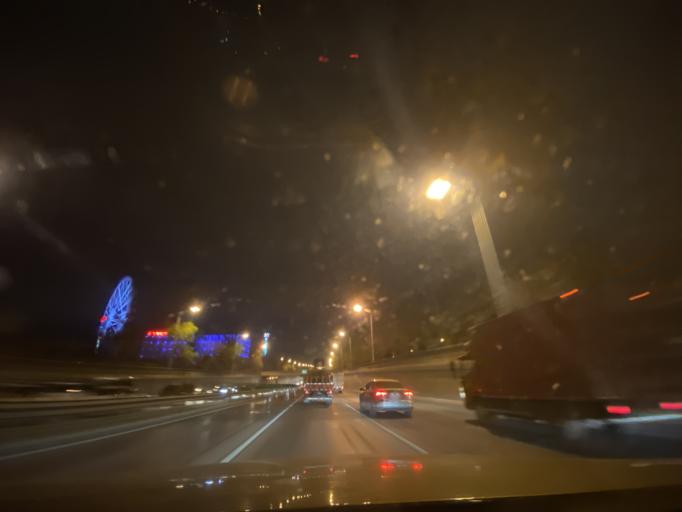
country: CN
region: Beijing
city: Lugu
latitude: 39.9111
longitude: 116.2051
